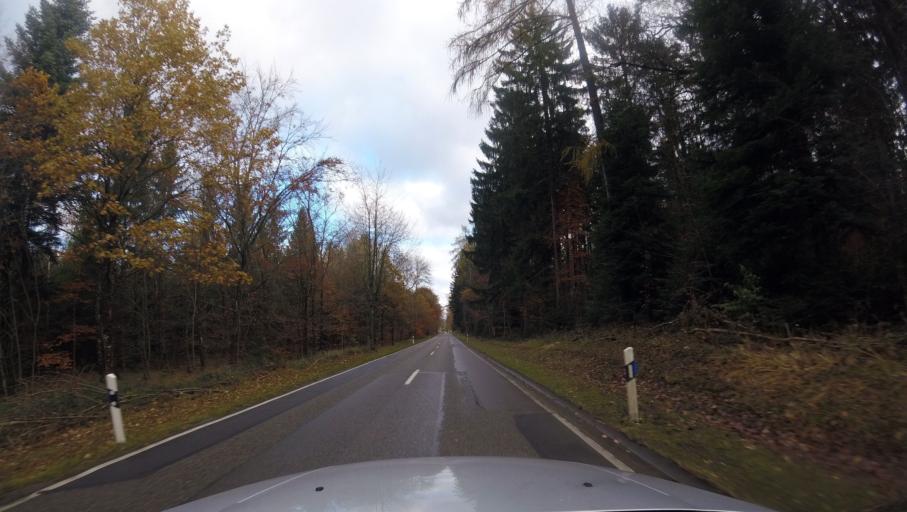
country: DE
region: Baden-Wuerttemberg
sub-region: Regierungsbezirk Stuttgart
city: Gschwend
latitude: 48.9490
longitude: 9.7294
